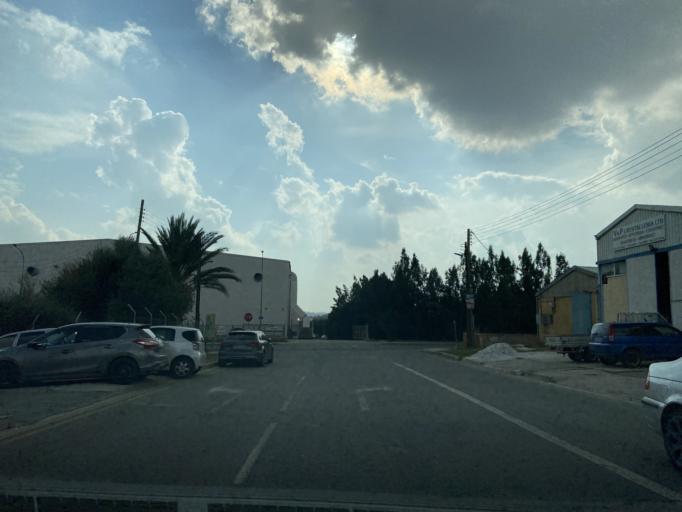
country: CY
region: Lefkosia
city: Dali
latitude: 35.0551
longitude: 33.3930
